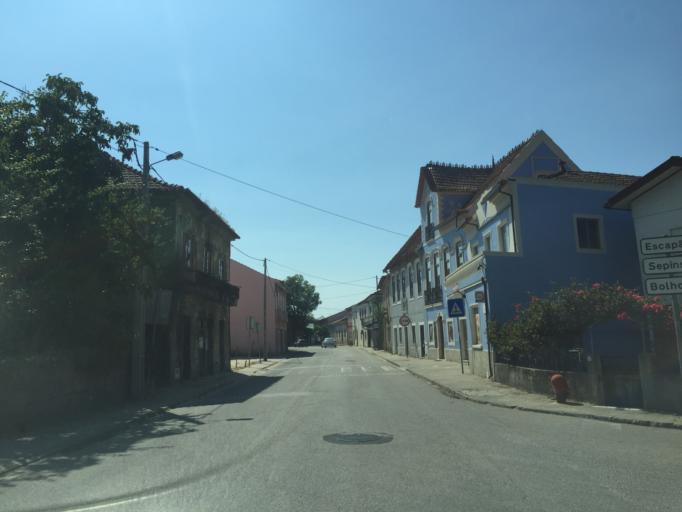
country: PT
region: Aveiro
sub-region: Mealhada
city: Mealhada
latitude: 40.3612
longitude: -8.5043
